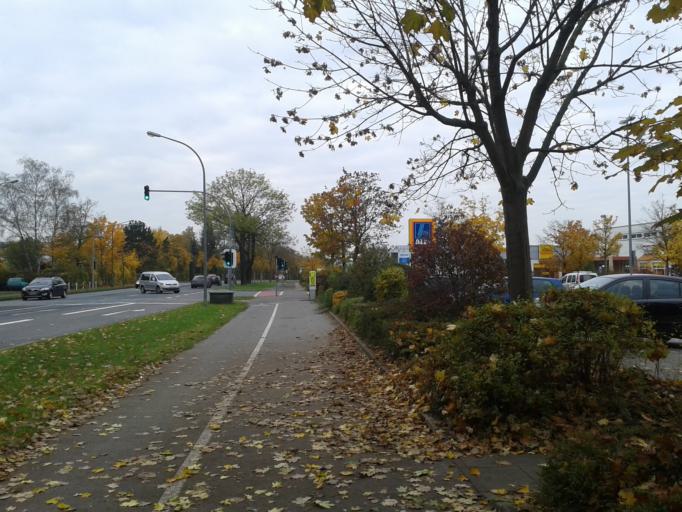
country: DE
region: Bavaria
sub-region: Upper Franconia
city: Bamberg
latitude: 49.9100
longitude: 10.9076
